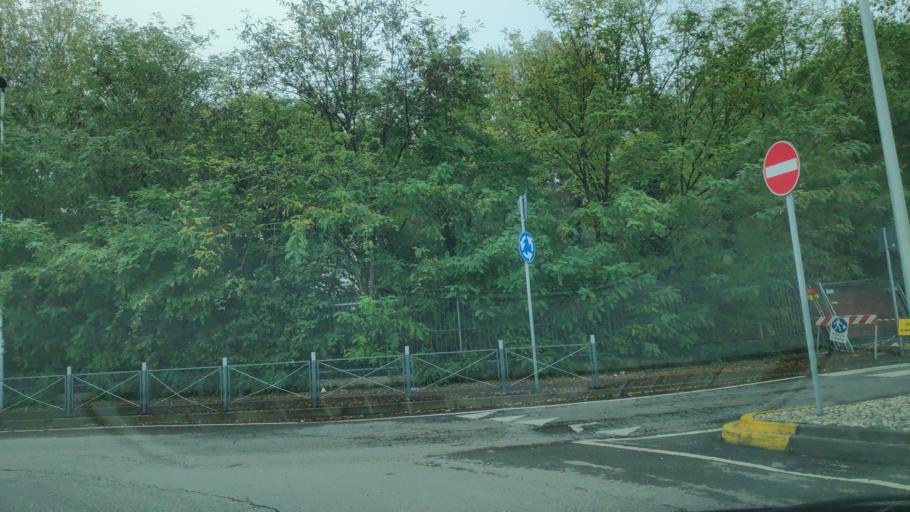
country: IT
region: Lombardy
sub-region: Citta metropolitana di Milano
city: Rozzano
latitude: 45.3787
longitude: 9.1699
